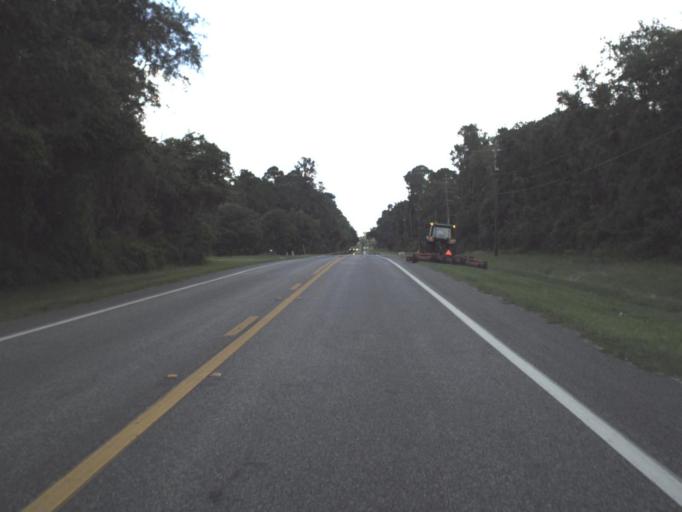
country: US
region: Florida
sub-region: Putnam County
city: Crescent City
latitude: 29.4598
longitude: -81.5211
